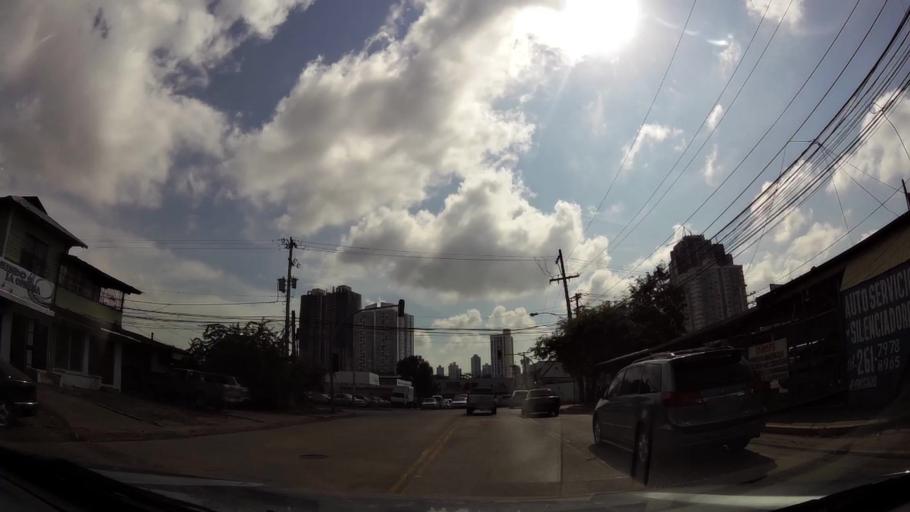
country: PA
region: Panama
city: Panama
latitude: 8.9990
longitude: -79.5211
